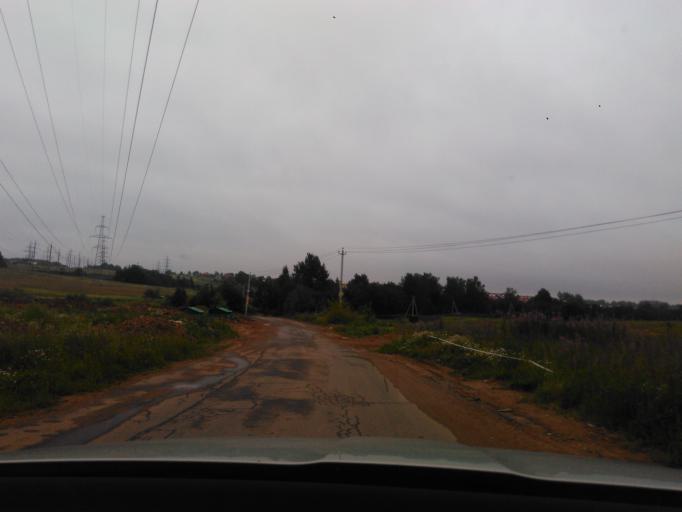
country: RU
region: Moskovskaya
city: Firsanovka
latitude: 55.9481
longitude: 37.2254
